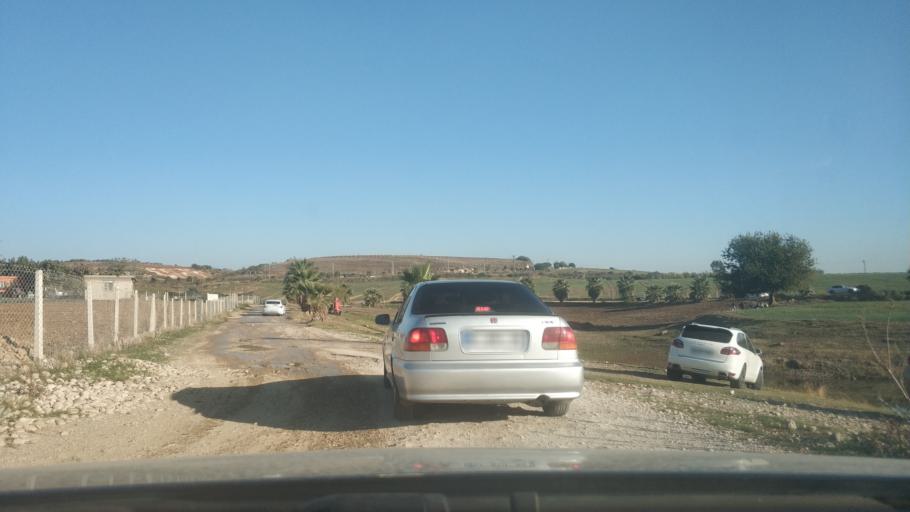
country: TR
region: Adana
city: Adana
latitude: 37.0940
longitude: 35.3006
